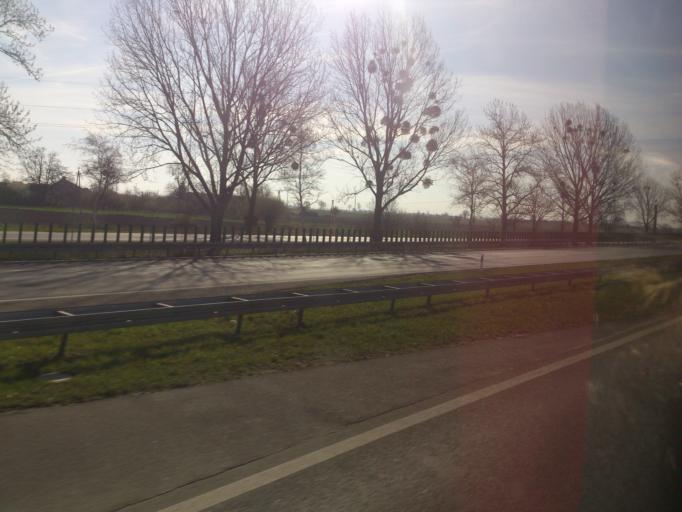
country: PL
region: Kujawsko-Pomorskie
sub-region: Powiat aleksandrowski
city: Raciazek
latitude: 52.8342
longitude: 18.7990
